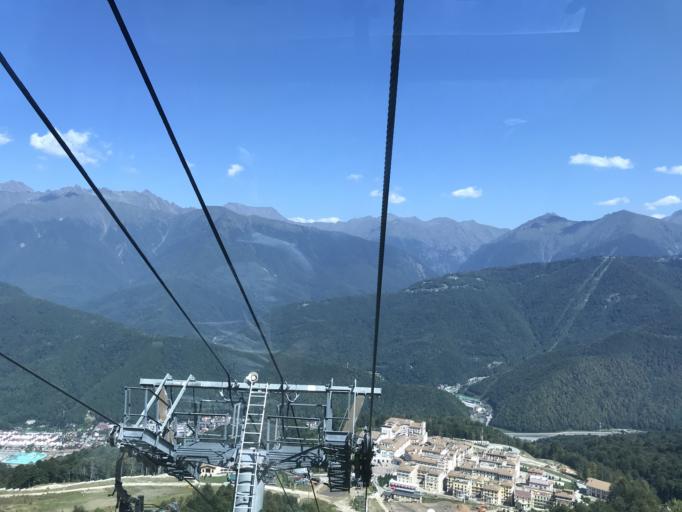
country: RU
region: Krasnodarskiy
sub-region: Sochi City
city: Krasnaya Polyana
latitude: 43.6633
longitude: 40.2544
